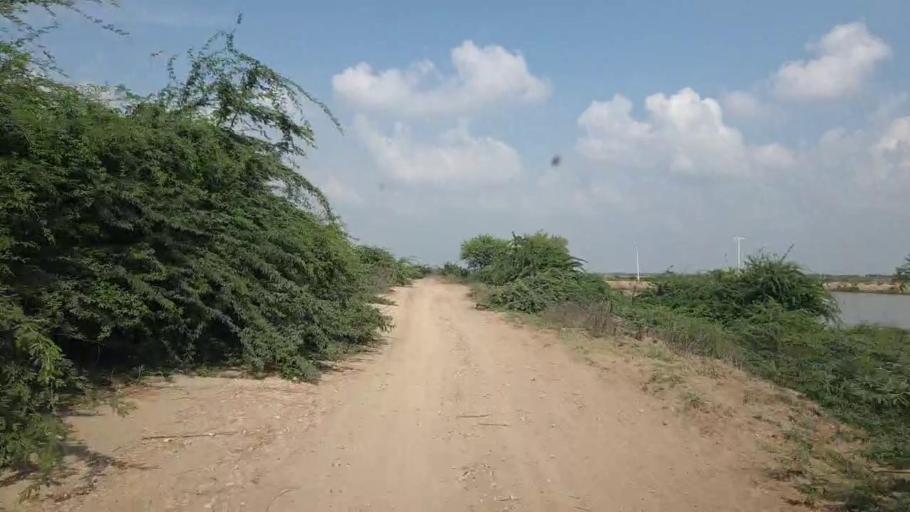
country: PK
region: Sindh
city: Badin
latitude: 24.4938
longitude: 68.6558
